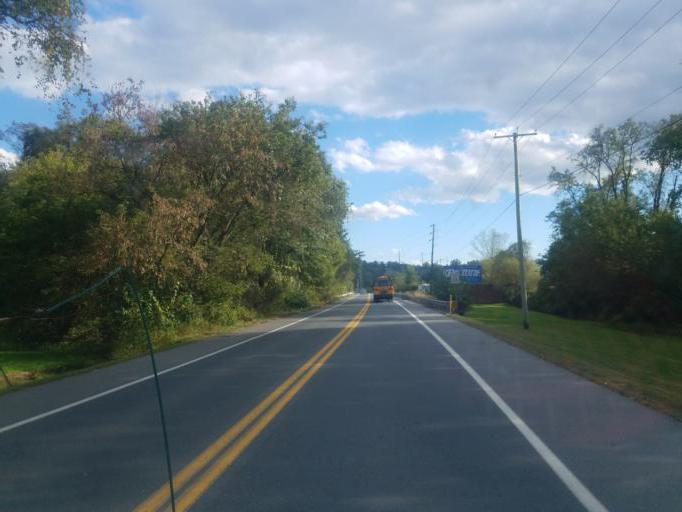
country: US
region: Pennsylvania
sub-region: Dauphin County
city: Middletown
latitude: 40.1848
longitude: -76.7277
